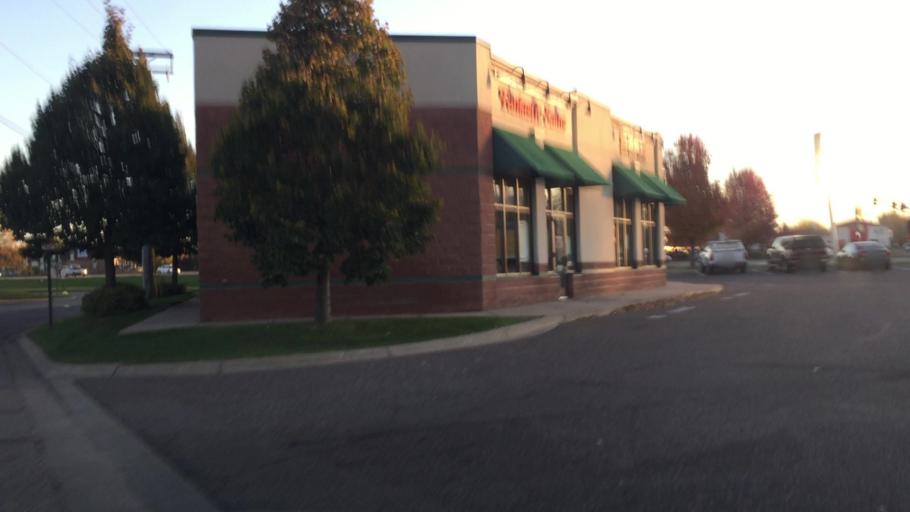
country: US
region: Minnesota
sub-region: Anoka County
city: Fridley
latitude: 45.1072
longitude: -93.2650
